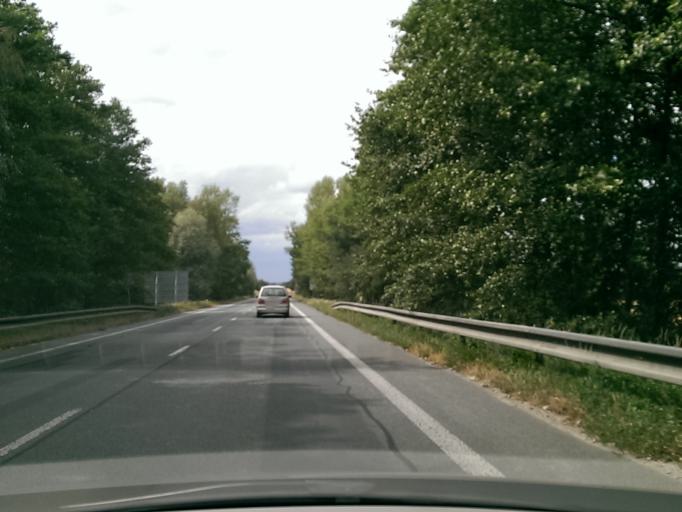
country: CZ
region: Central Bohemia
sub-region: Okres Nymburk
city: Podebrady
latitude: 50.1225
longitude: 15.1164
